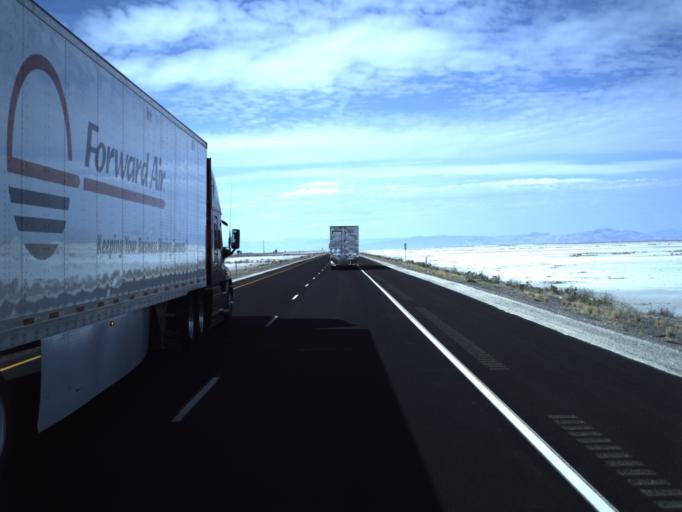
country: US
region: Utah
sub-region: Tooele County
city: Wendover
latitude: 40.7316
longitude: -113.4914
